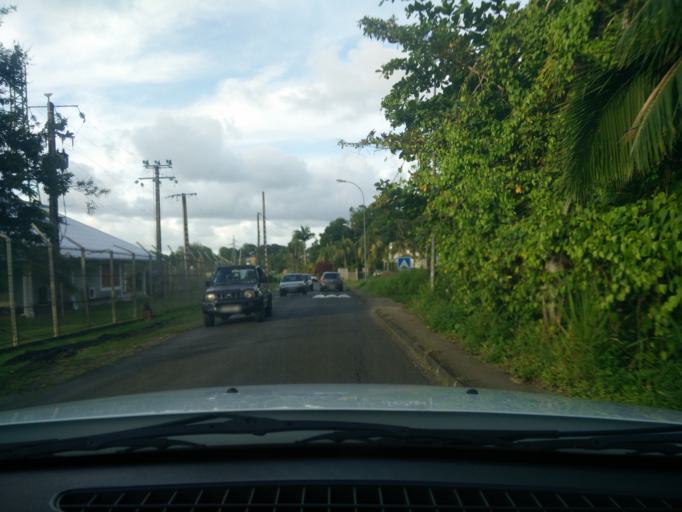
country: GP
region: Guadeloupe
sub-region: Guadeloupe
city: Les Abymes
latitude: 16.2521
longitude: -61.5082
